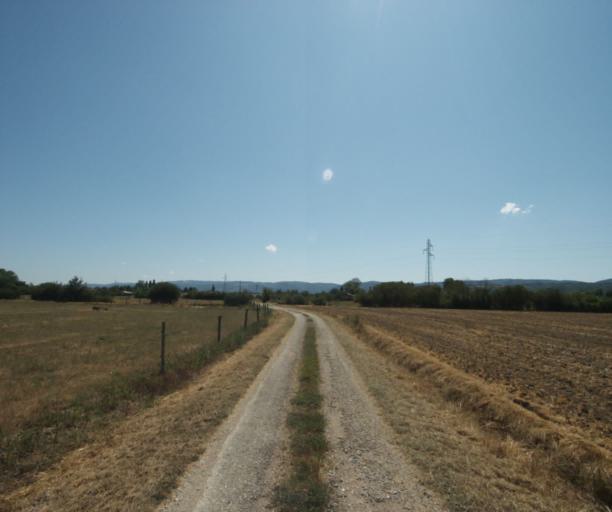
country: FR
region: Midi-Pyrenees
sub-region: Departement de la Haute-Garonne
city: Revel
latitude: 43.4690
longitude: 1.9870
